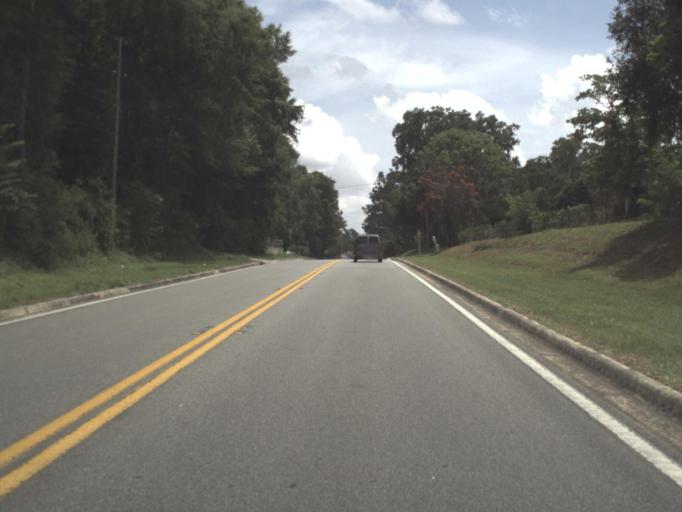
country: US
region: Florida
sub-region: Madison County
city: Madison
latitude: 30.4756
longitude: -83.4157
